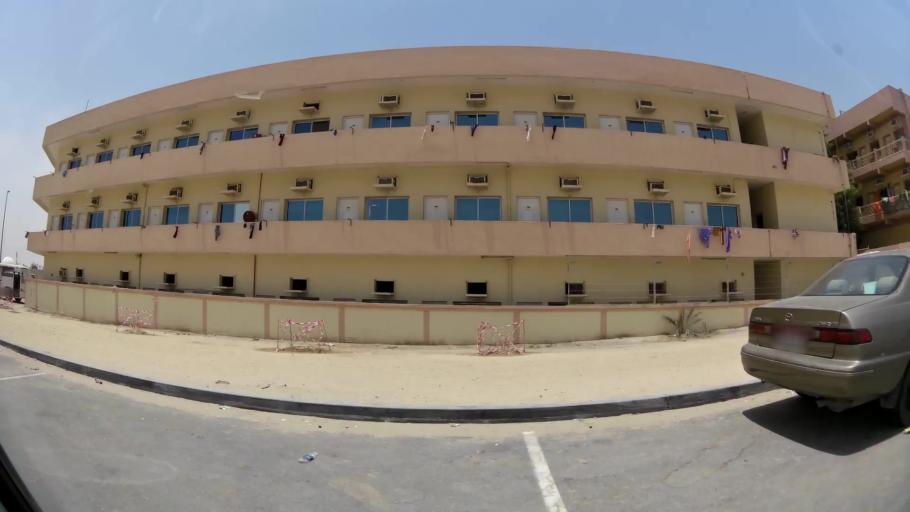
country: AE
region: Ash Shariqah
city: Sharjah
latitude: 25.2761
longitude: 55.4259
